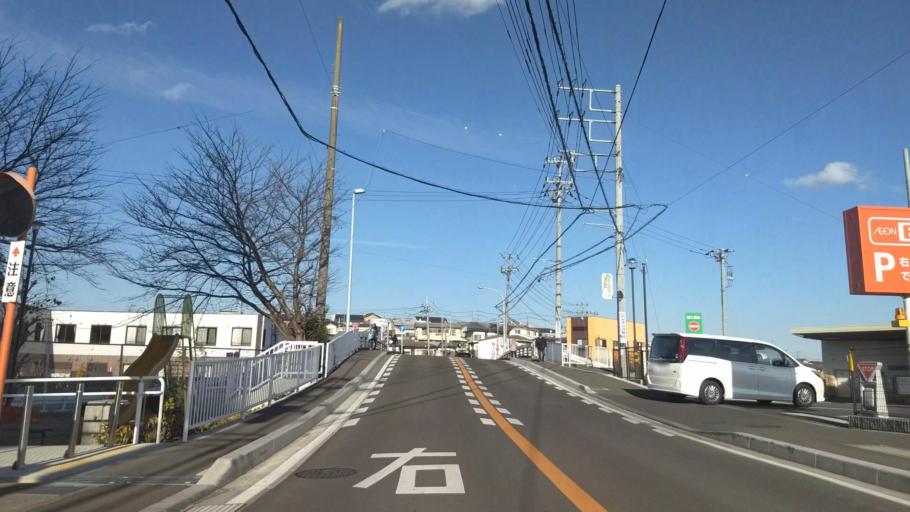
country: JP
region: Kanagawa
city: Isehara
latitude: 35.3728
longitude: 139.2746
